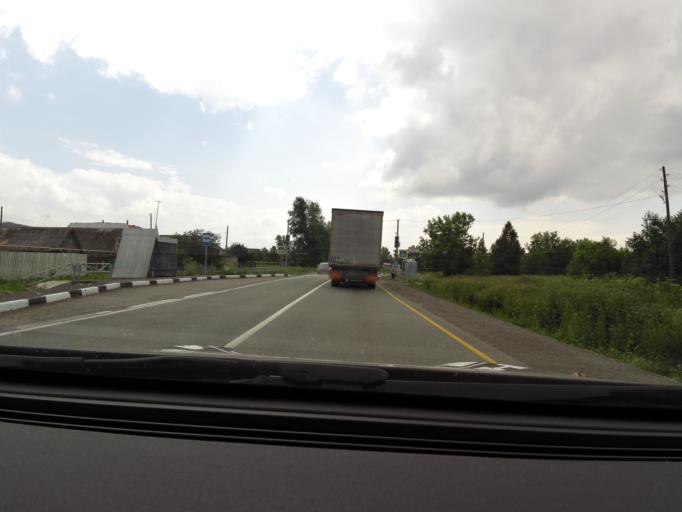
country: RU
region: Perm
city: Suksun
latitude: 57.0606
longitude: 57.4255
